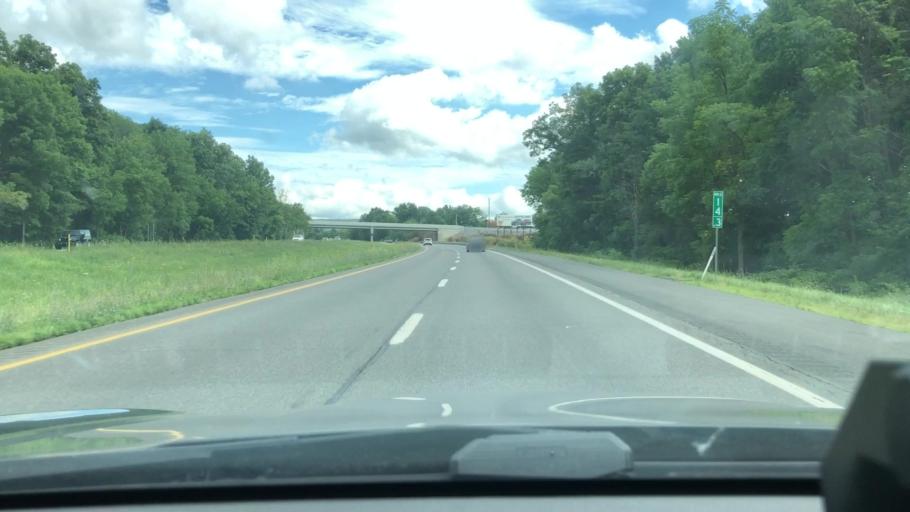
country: US
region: Pennsylvania
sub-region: Northampton County
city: Wind Gap
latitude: 40.8172
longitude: -75.2987
